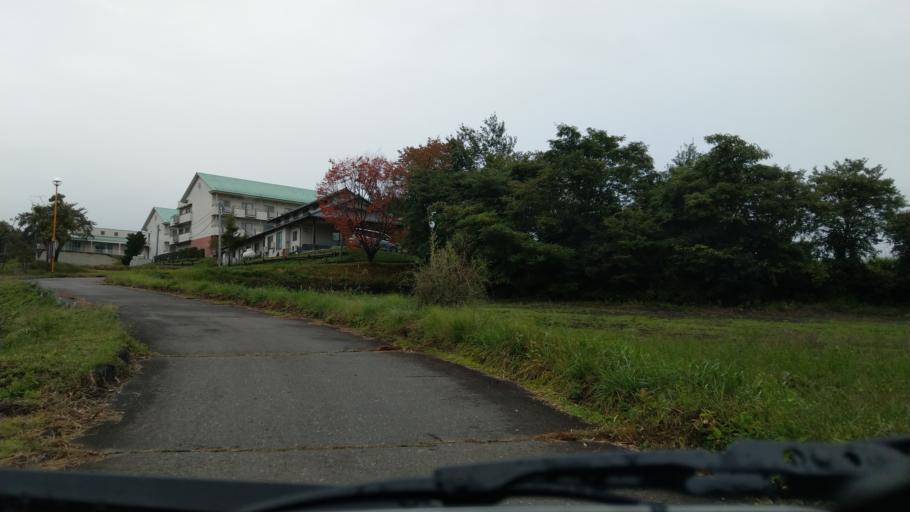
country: JP
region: Nagano
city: Komoro
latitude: 36.3367
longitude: 138.4529
